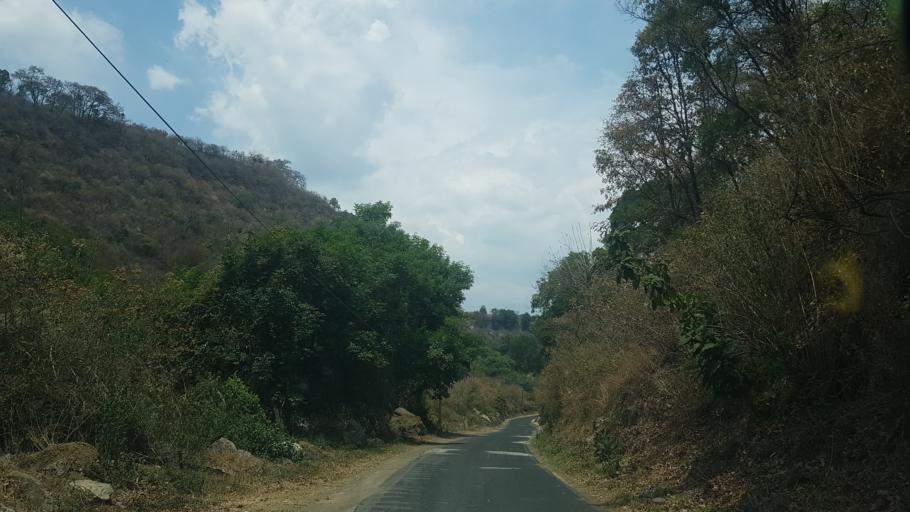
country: MX
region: Puebla
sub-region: Tochimilco
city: La Magdalena Yancuitlalpan
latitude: 18.8742
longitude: -98.6099
